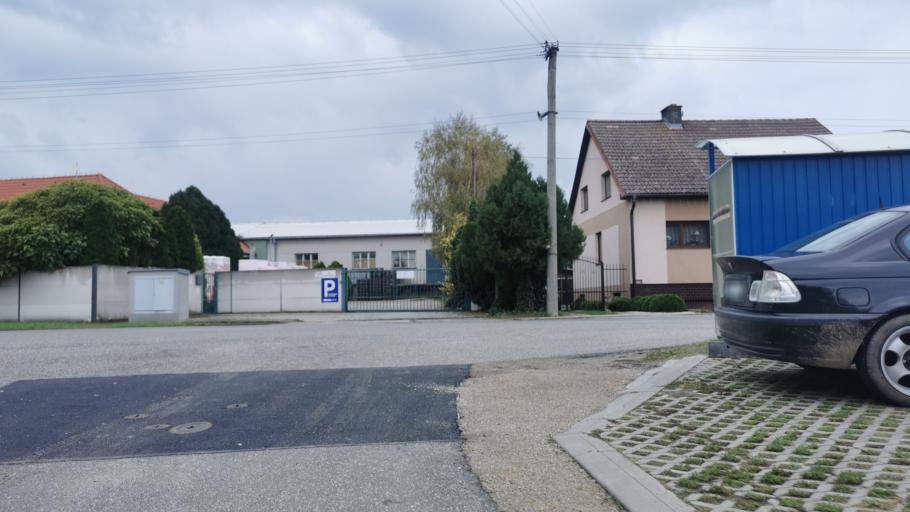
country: SK
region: Trnavsky
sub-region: Okres Skalica
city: Holic
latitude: 48.8193
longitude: 17.1945
